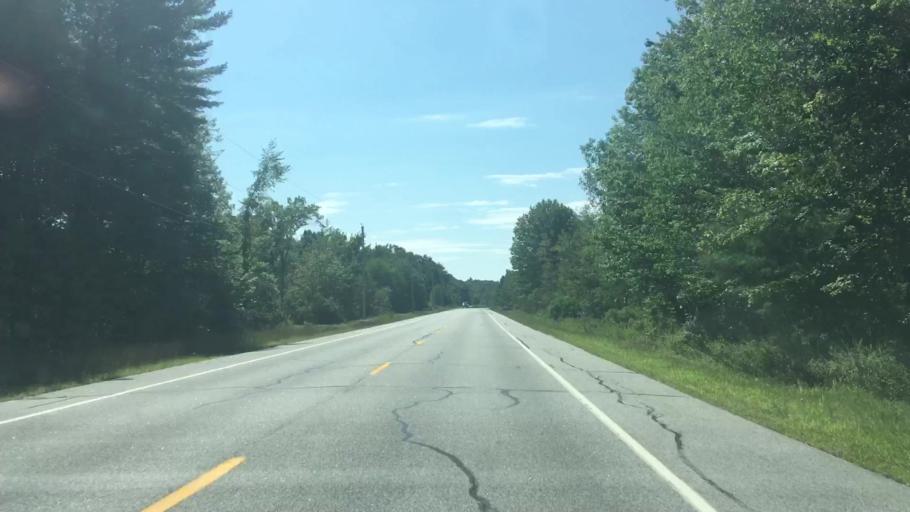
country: US
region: Maine
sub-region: Androscoggin County
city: Sabattus
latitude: 44.1452
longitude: -70.0421
